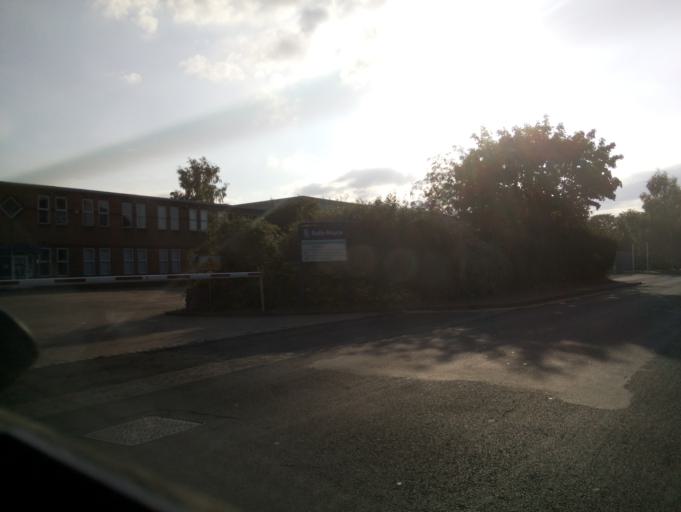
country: GB
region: England
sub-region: Gloucestershire
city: Barnwood
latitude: 51.8652
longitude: -2.2028
